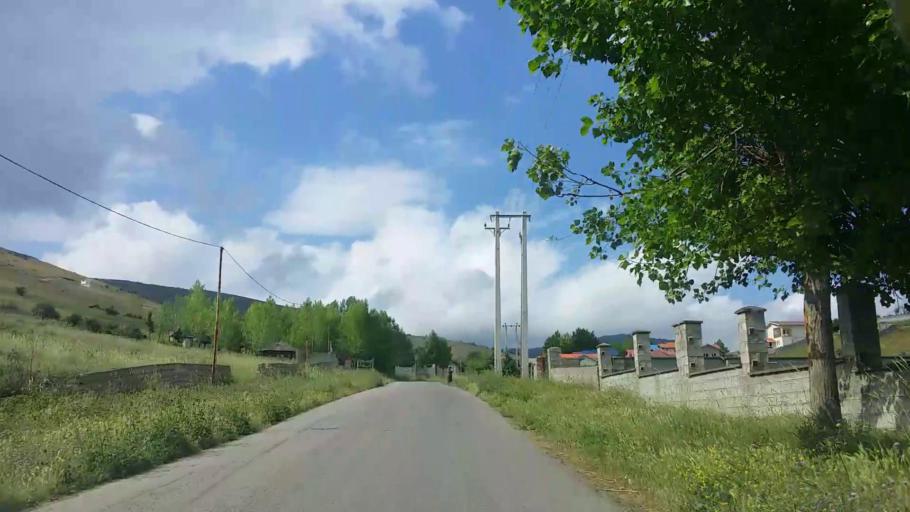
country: IR
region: Mazandaran
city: Chalus
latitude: 36.5303
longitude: 51.2689
